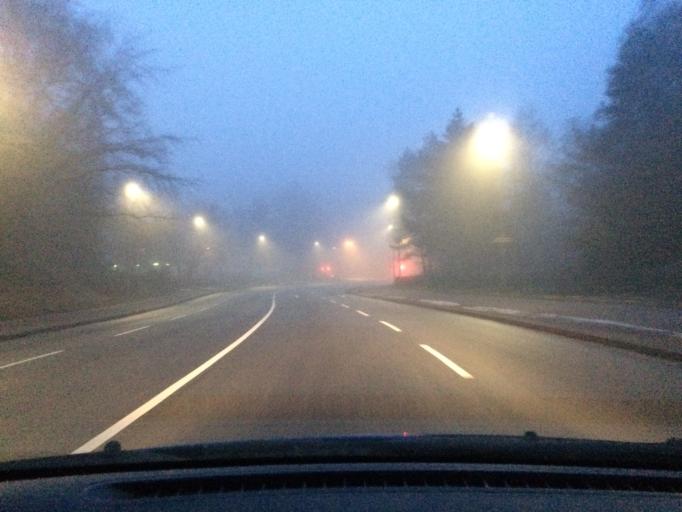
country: DE
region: Schleswig-Holstein
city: Geesthacht
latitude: 53.4375
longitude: 10.3873
